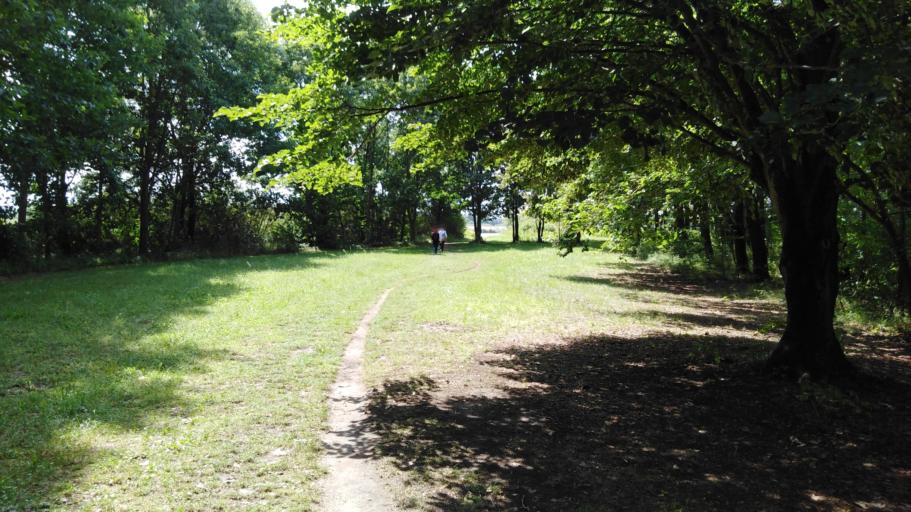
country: HU
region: Zala
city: Zalakomar
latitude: 46.6058
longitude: 17.1669
